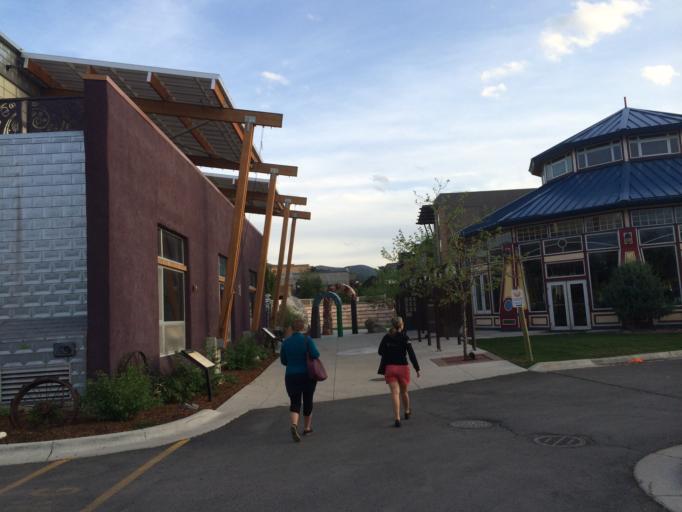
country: US
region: Montana
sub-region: Lewis and Clark County
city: Helena
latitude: 46.5979
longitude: -112.0363
